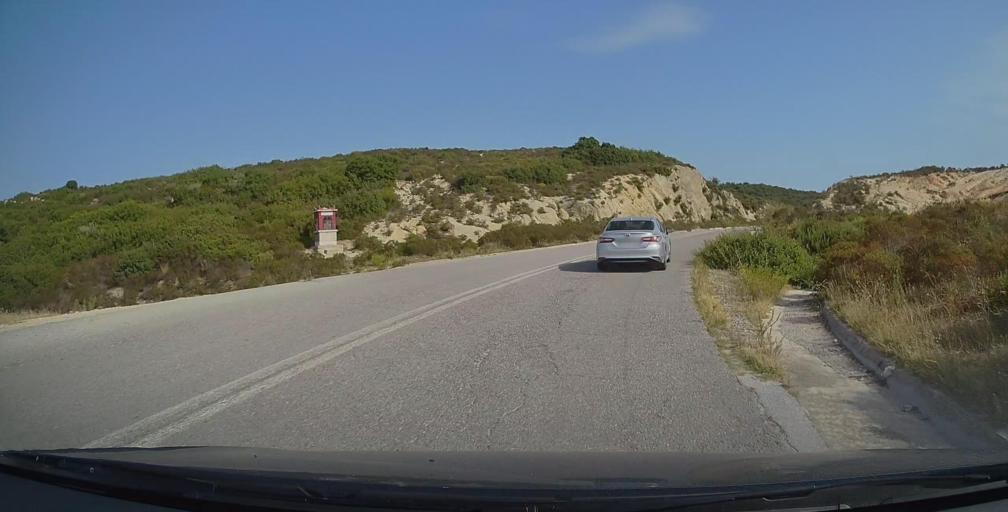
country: GR
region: Central Macedonia
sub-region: Nomos Chalkidikis
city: Sykia
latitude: 39.9799
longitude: 23.9586
